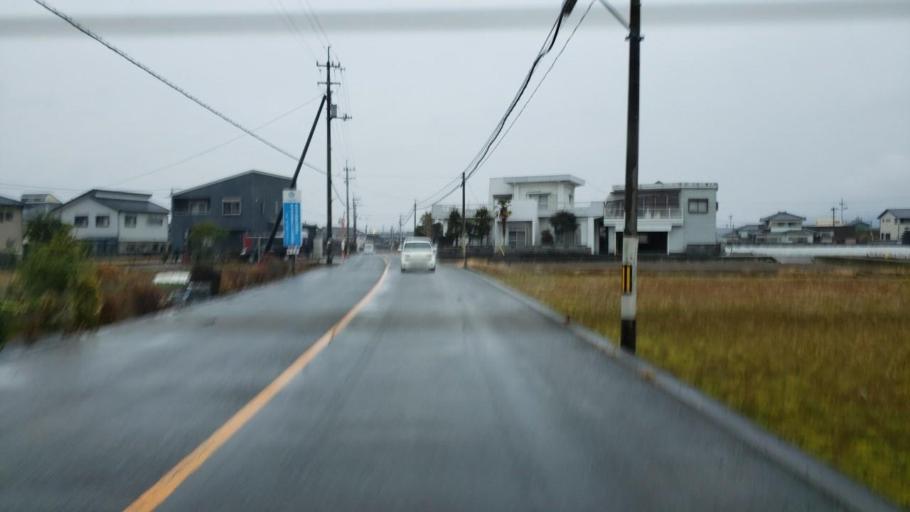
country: JP
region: Tokushima
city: Kamojimacho-jogejima
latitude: 34.0969
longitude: 134.3561
